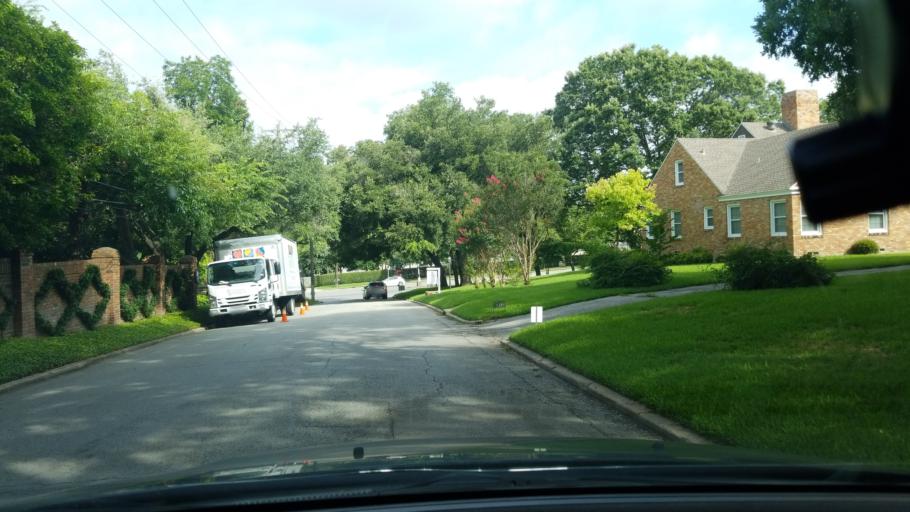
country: US
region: Texas
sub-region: Dallas County
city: Highland Park
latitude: 32.8184
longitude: -96.7173
